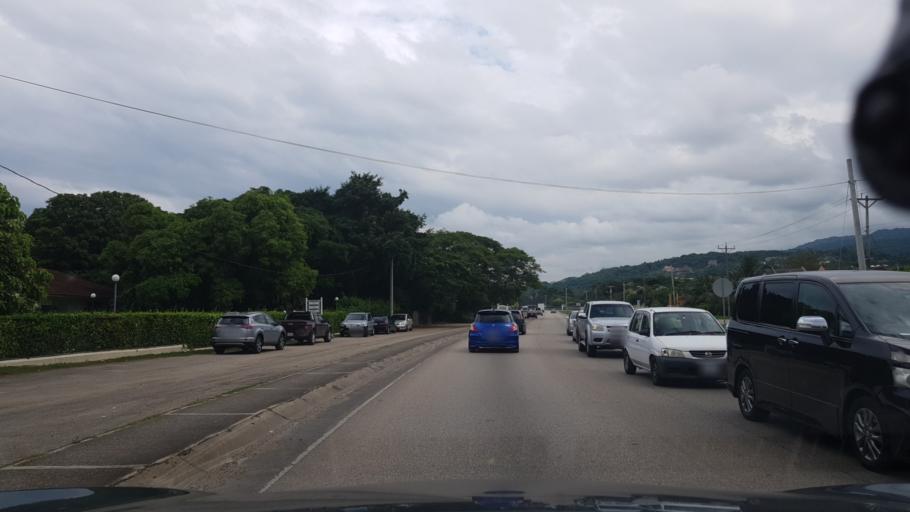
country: JM
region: Saint Ann
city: Runaway Bay
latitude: 18.4635
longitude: -77.3329
